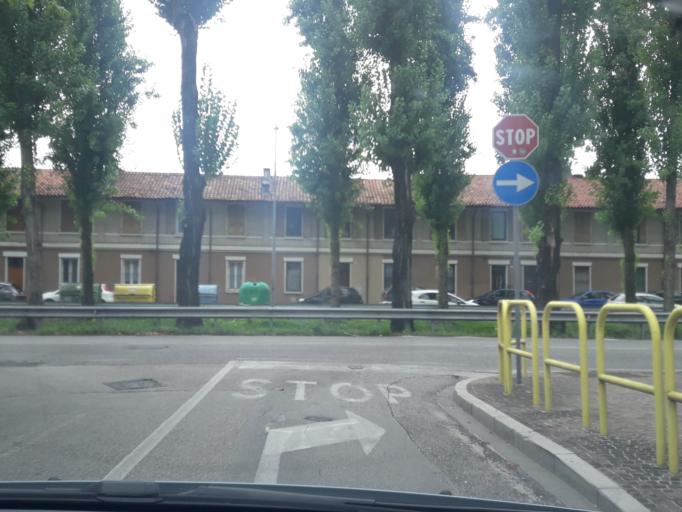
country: IT
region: Friuli Venezia Giulia
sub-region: Provincia di Udine
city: Udine
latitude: 46.0721
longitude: 13.2264
